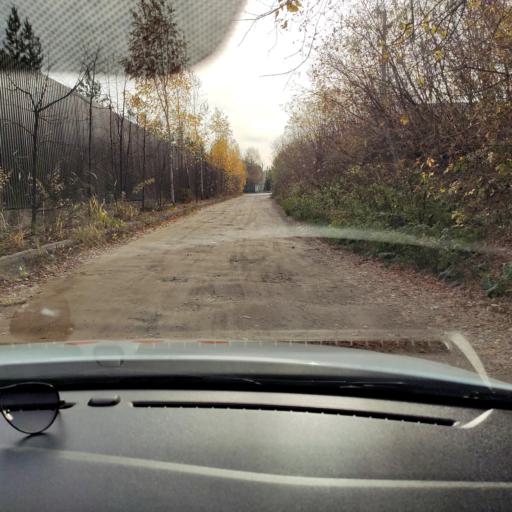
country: RU
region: Tatarstan
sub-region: Gorod Kazan'
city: Kazan
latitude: 55.8084
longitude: 49.0610
